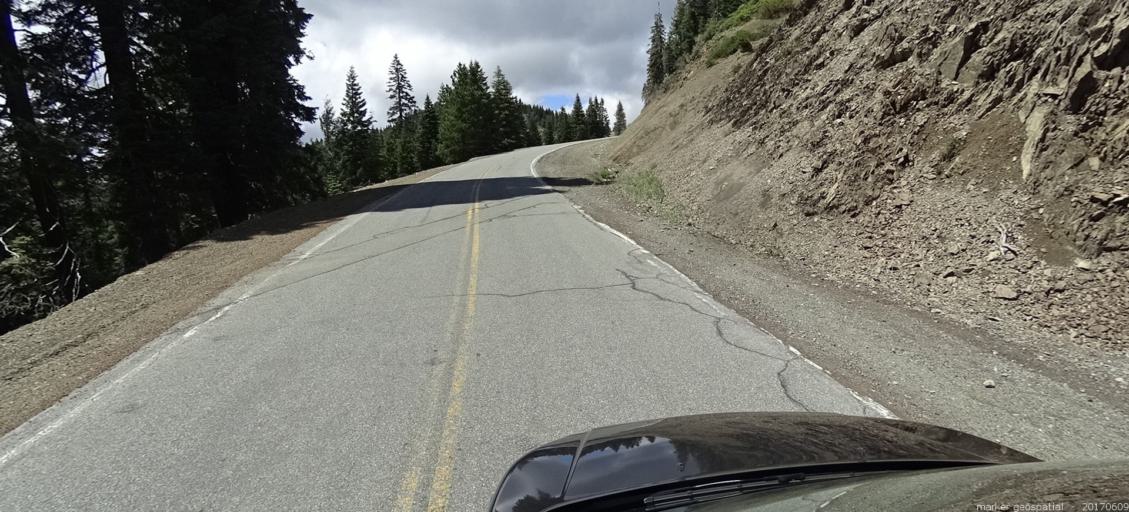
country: US
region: California
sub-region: Siskiyou County
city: Yreka
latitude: 41.3913
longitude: -122.9920
